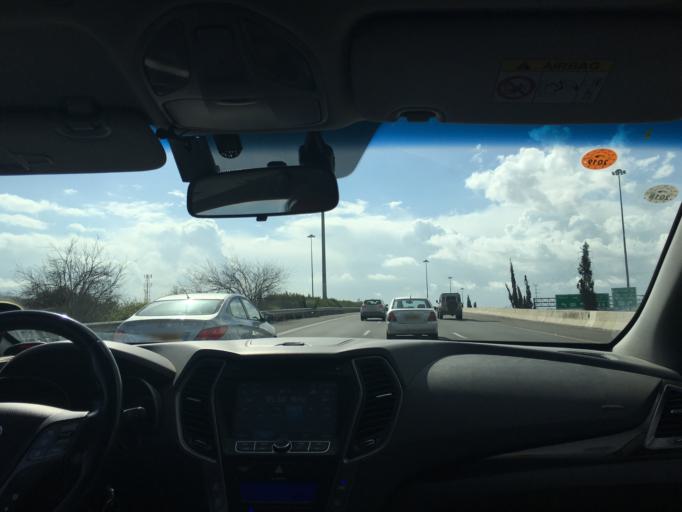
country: IL
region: Tel Aviv
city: Azor
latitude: 32.0400
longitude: 34.8296
